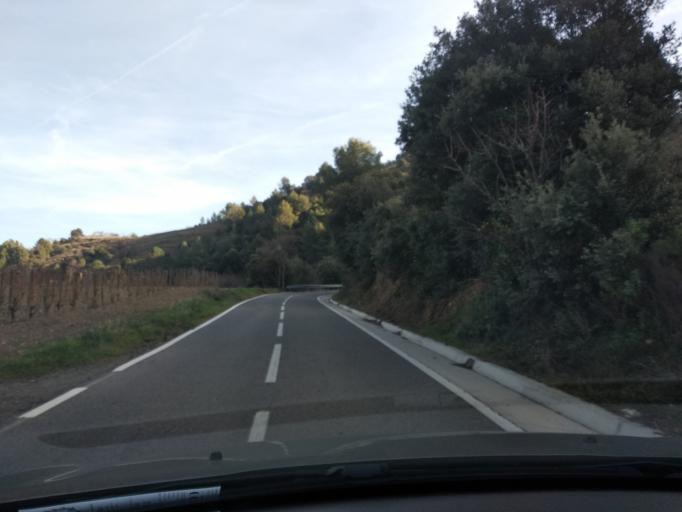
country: ES
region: Catalonia
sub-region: Provincia de Tarragona
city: la Morera de Montsant
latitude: 41.2453
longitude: 0.8028
